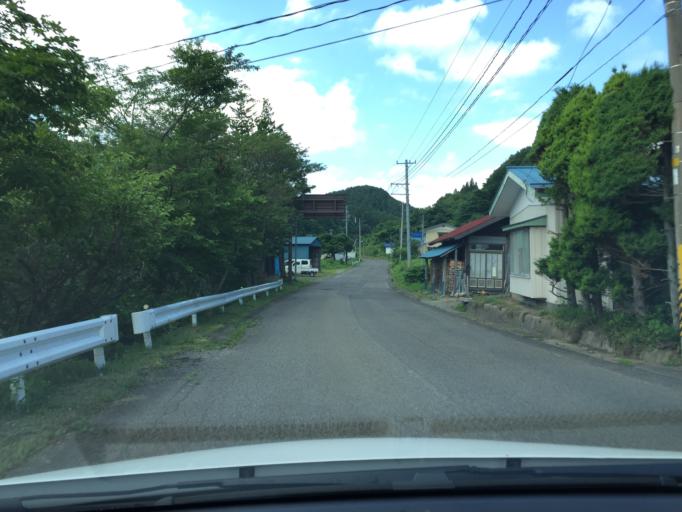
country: JP
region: Fukushima
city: Inawashiro
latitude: 37.2800
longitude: 140.0617
